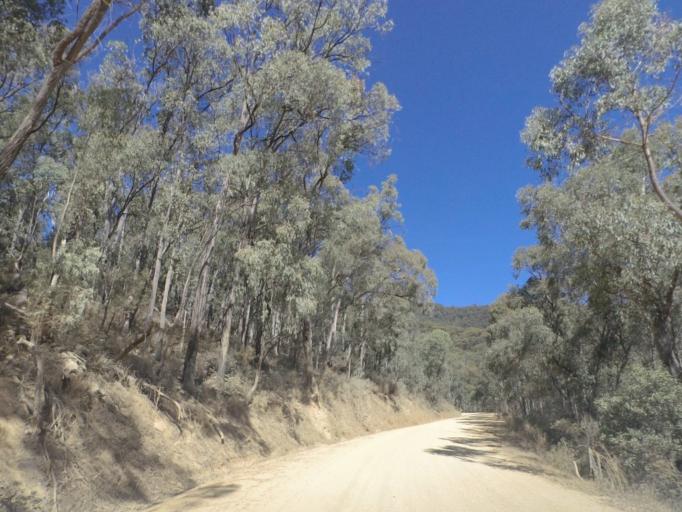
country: AU
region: Victoria
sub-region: Murrindindi
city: Alexandra
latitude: -37.3206
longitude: 145.8104
